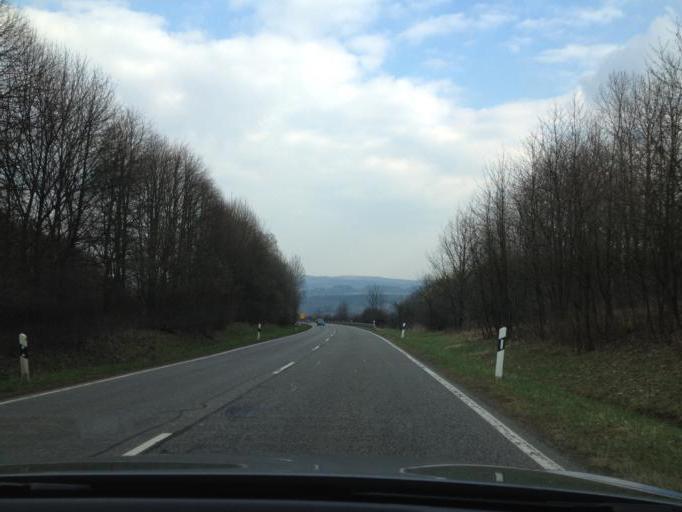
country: DE
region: Saarland
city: Freisen
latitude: 49.5429
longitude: 7.2597
